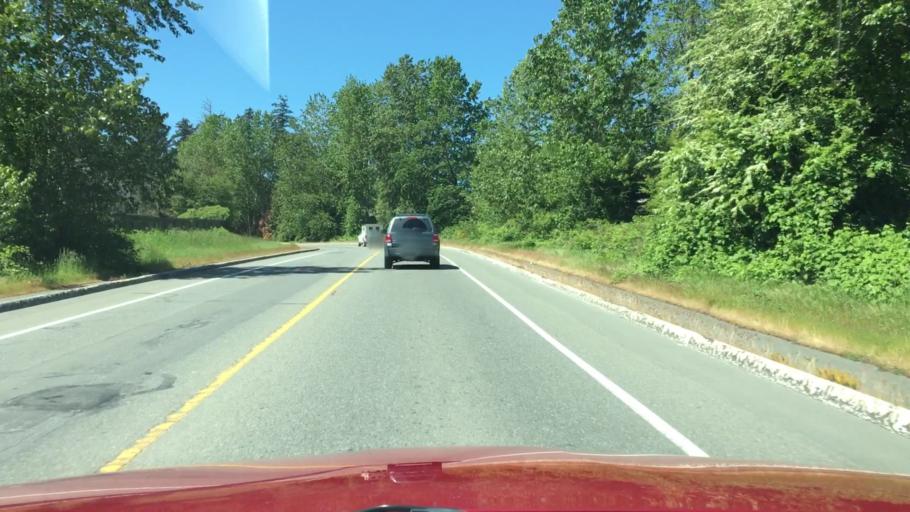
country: CA
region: British Columbia
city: Victoria
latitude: 48.4742
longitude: -123.4158
